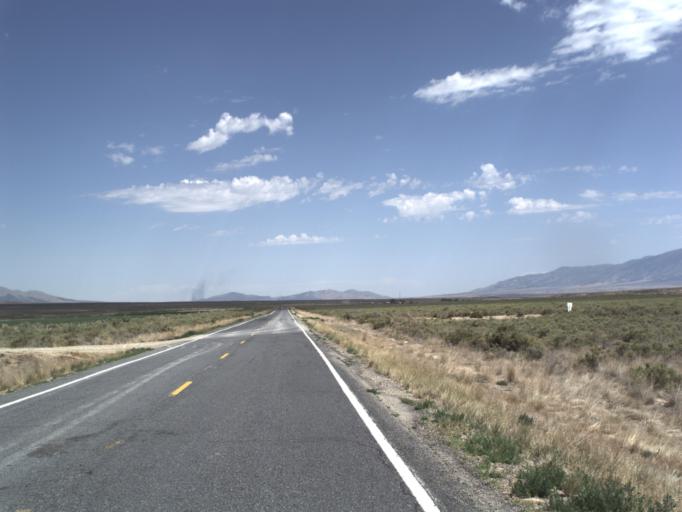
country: US
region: Utah
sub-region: Tooele County
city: Tooele
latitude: 40.1408
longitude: -112.4308
